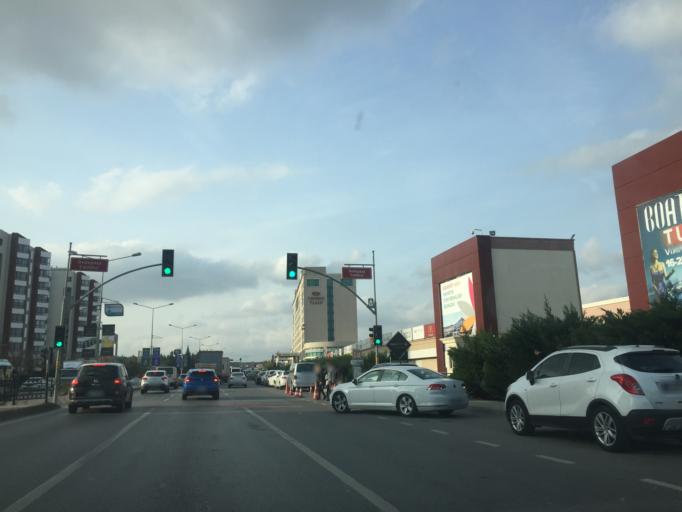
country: TR
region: Istanbul
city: Sultanbeyli
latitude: 40.9366
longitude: 29.3251
